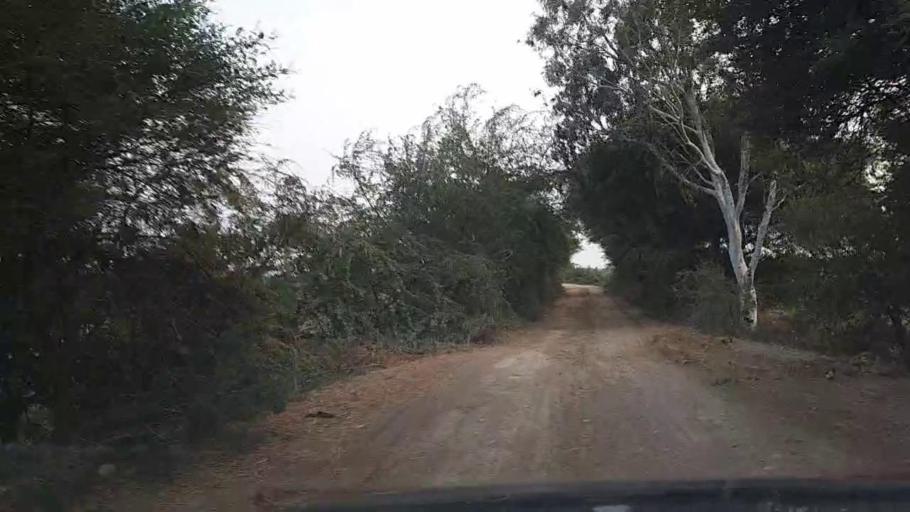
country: PK
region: Sindh
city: Gharo
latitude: 24.7432
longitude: 67.6937
